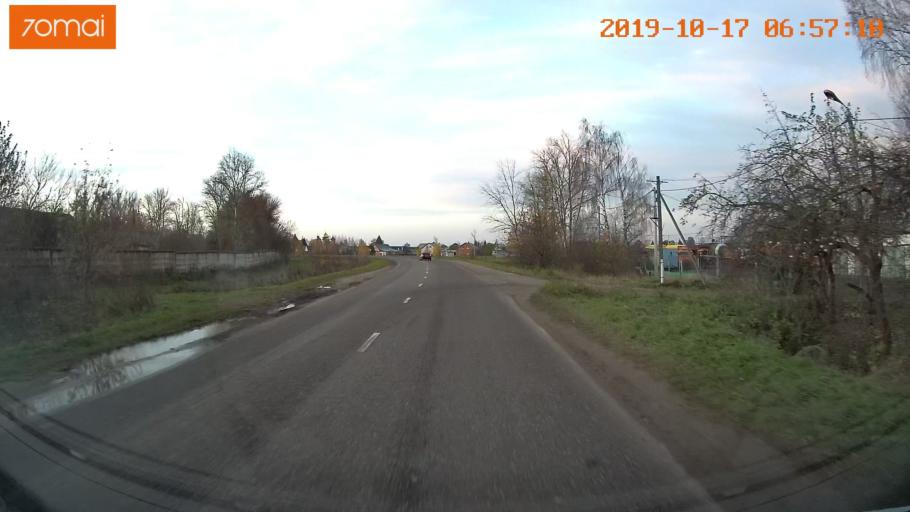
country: RU
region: Vladimir
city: Suzdal'
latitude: 56.4390
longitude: 40.4414
